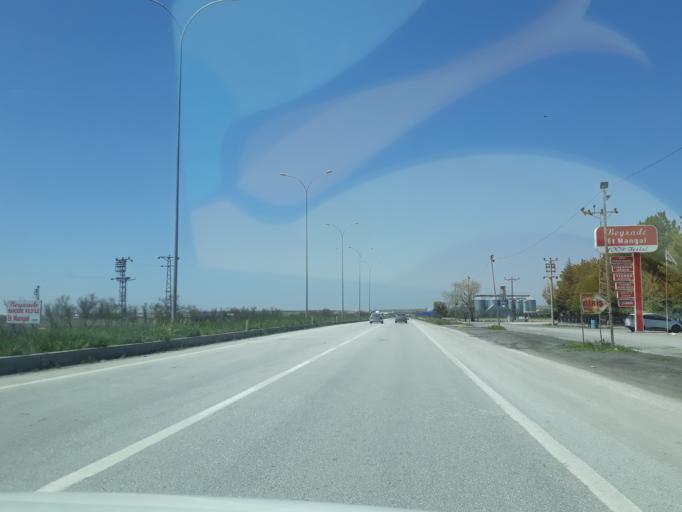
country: TR
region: Konya
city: Karapinar
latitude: 37.7151
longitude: 33.5117
